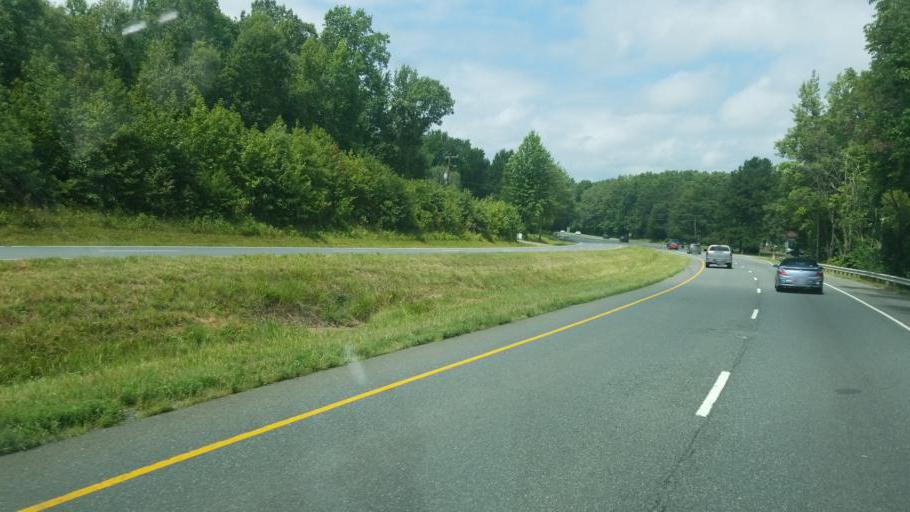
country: US
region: Virginia
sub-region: Stafford County
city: Falmouth
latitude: 38.3890
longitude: -77.5480
